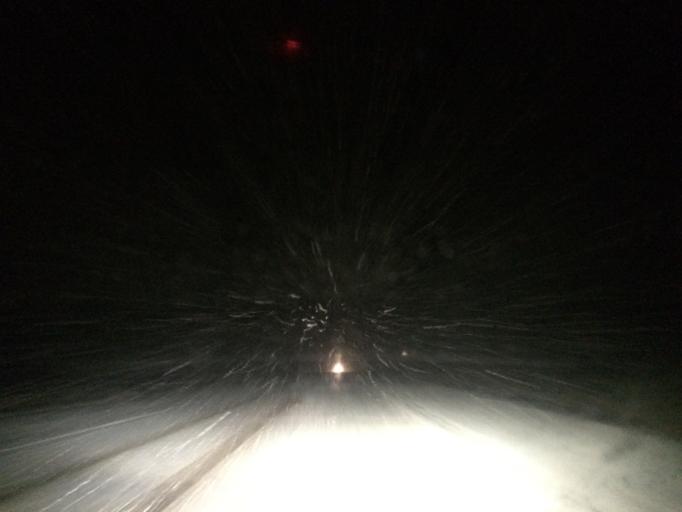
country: RU
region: Tula
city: Krapivna
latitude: 54.1152
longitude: 37.2209
